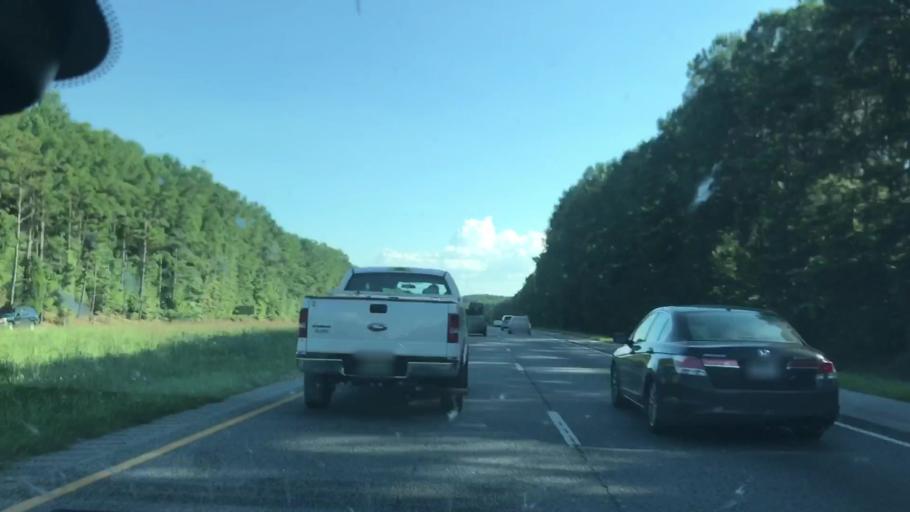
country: US
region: Georgia
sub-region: Harris County
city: Hamilton
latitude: 32.8048
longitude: -85.0215
